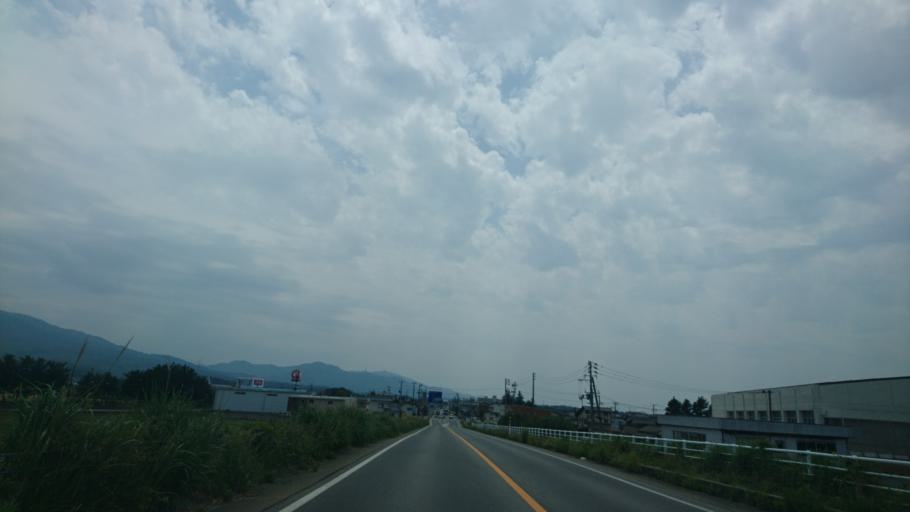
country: JP
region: Niigata
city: Murakami
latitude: 38.1231
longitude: 139.4536
